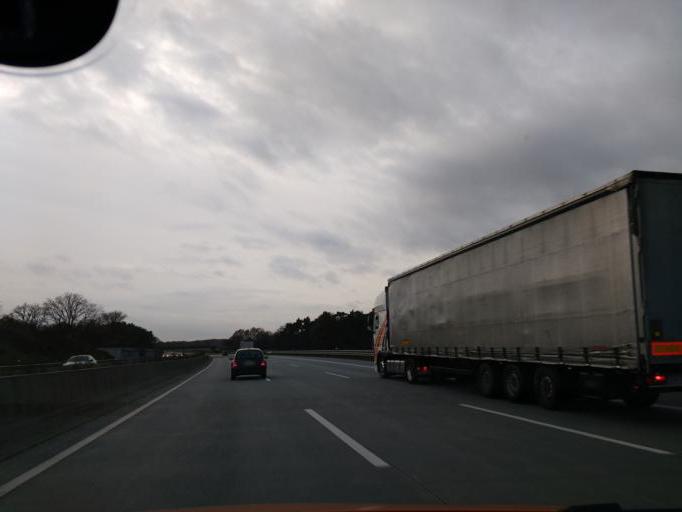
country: DE
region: Lower Saxony
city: Sittensen
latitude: 53.2879
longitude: 9.4897
